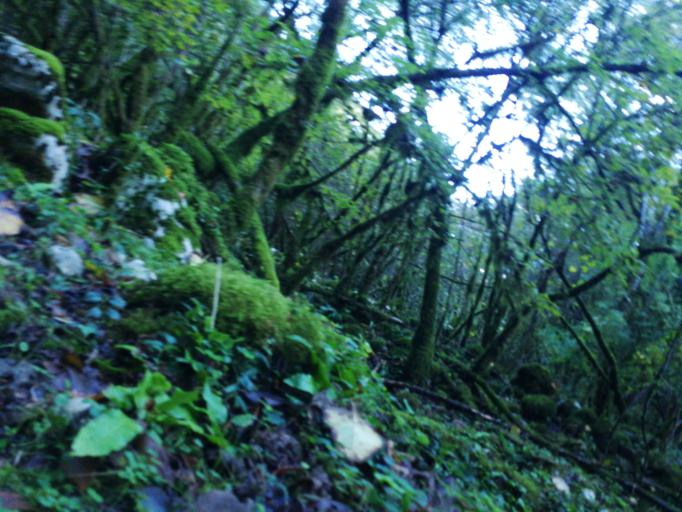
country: GE
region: Abkhazia
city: Gagra
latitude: 43.3250
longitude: 40.2553
